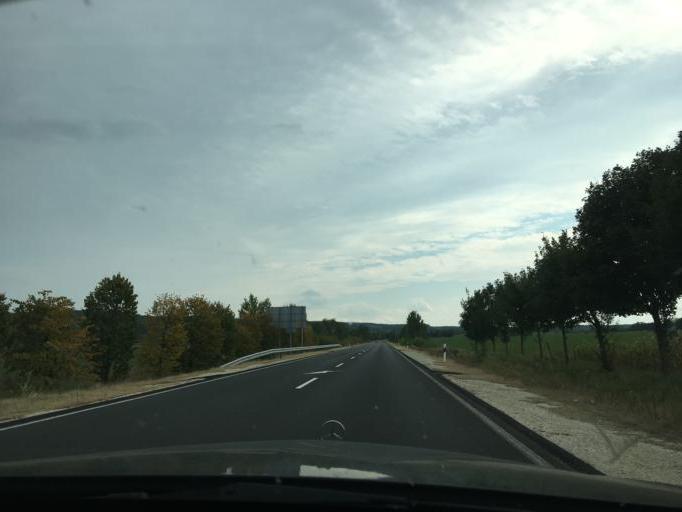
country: HU
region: Somogy
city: Balatonszarszo
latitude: 46.8311
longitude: 17.8491
